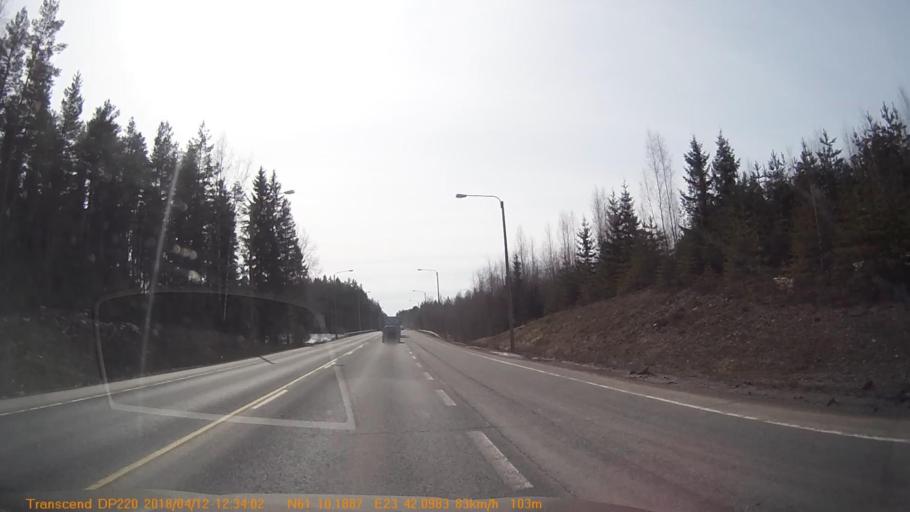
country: FI
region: Pirkanmaa
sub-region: Etelae-Pirkanmaa
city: Kylmaekoski
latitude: 61.1695
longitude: 23.7014
